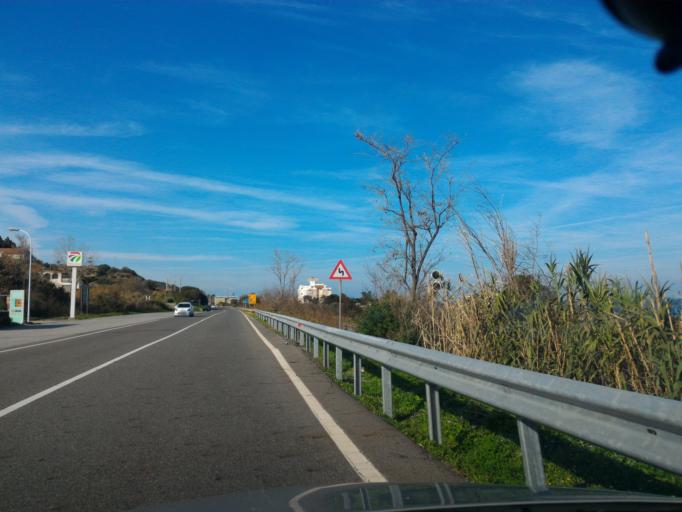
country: IT
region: Calabria
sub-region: Provincia di Crotone
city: Torretta
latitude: 39.4355
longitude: 17.0549
